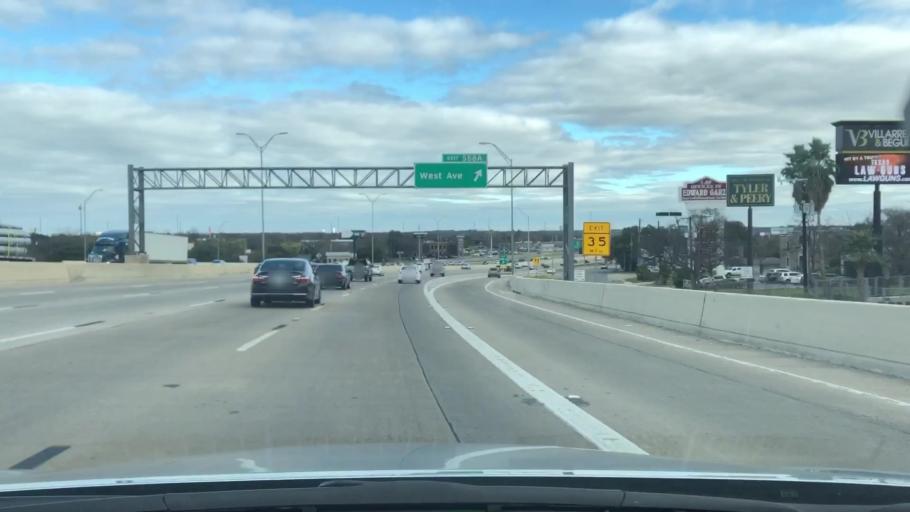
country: US
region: Texas
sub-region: Bexar County
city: Balcones Heights
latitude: 29.4856
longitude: -98.5329
